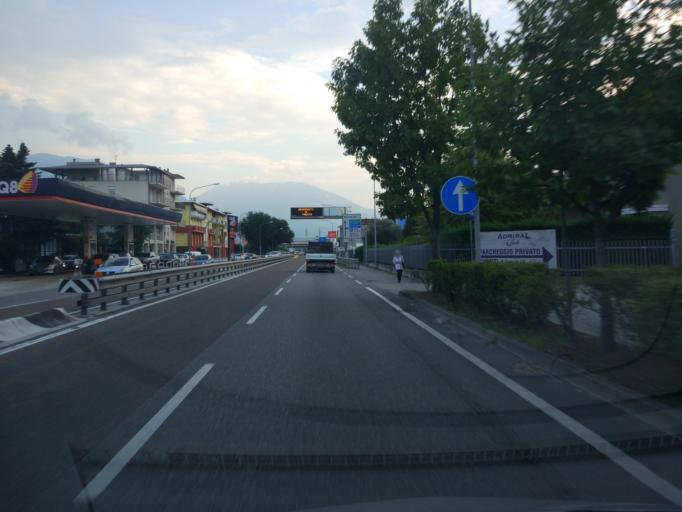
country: IT
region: Trentino-Alto Adige
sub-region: Provincia di Trento
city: Meano
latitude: 46.1004
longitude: 11.1114
